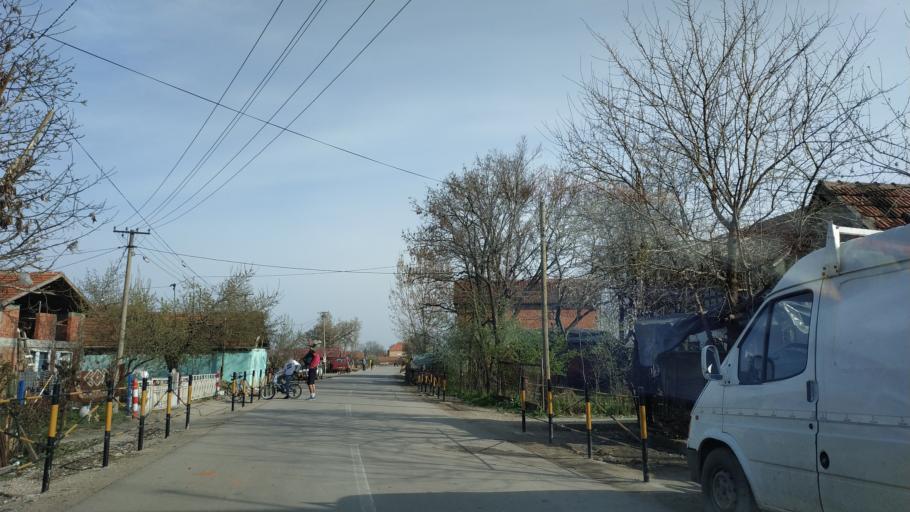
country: RS
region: Central Serbia
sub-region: Nisavski Okrug
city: Aleksinac
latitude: 43.5159
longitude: 21.6917
